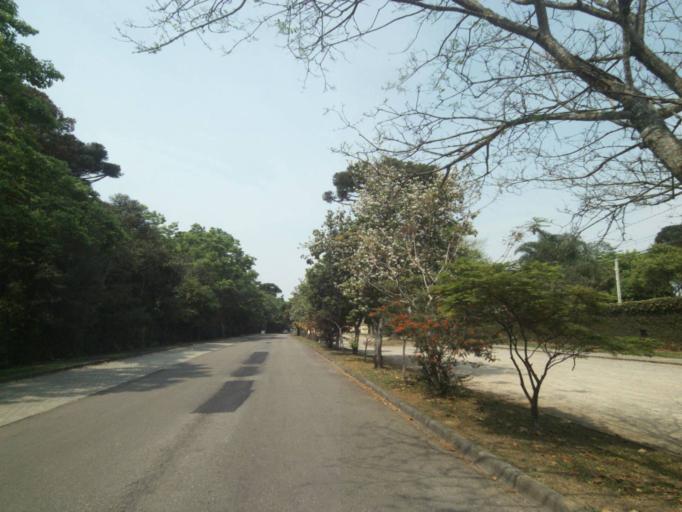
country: BR
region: Parana
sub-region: Sao Jose Dos Pinhais
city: Sao Jose dos Pinhais
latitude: -25.4898
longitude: -49.2089
